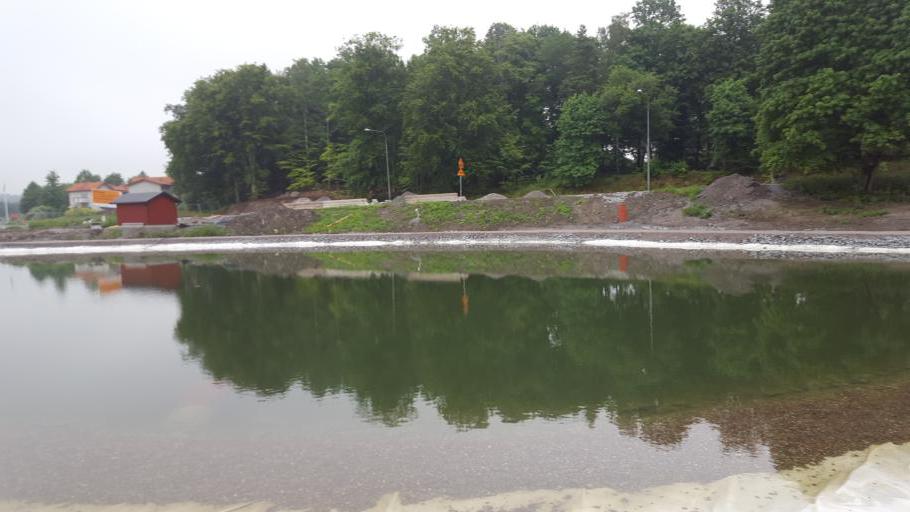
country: SE
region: Stockholm
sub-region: Upplands Vasby Kommun
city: Upplands Vaesby
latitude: 59.5093
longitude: 17.8807
